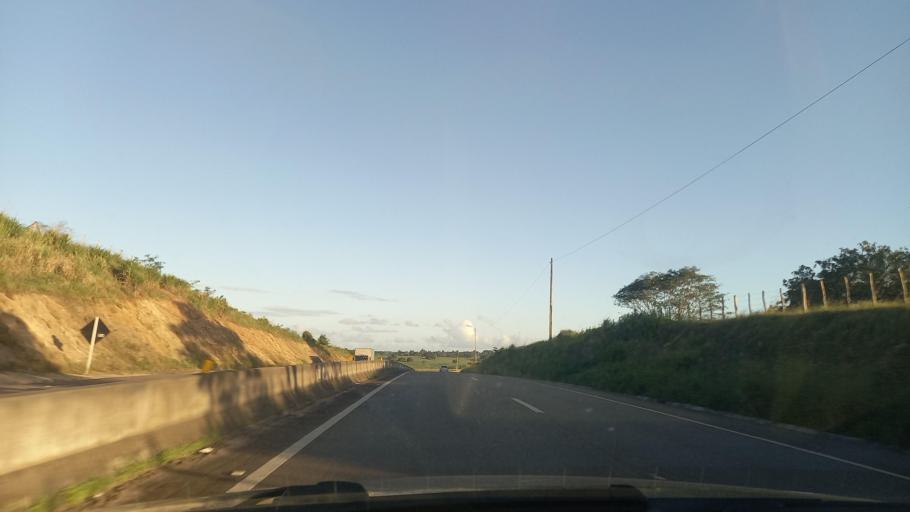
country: BR
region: Alagoas
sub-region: Limoeiro De Anadia
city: Limoeiro de Anadia
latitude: -9.7517
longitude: -36.5034
